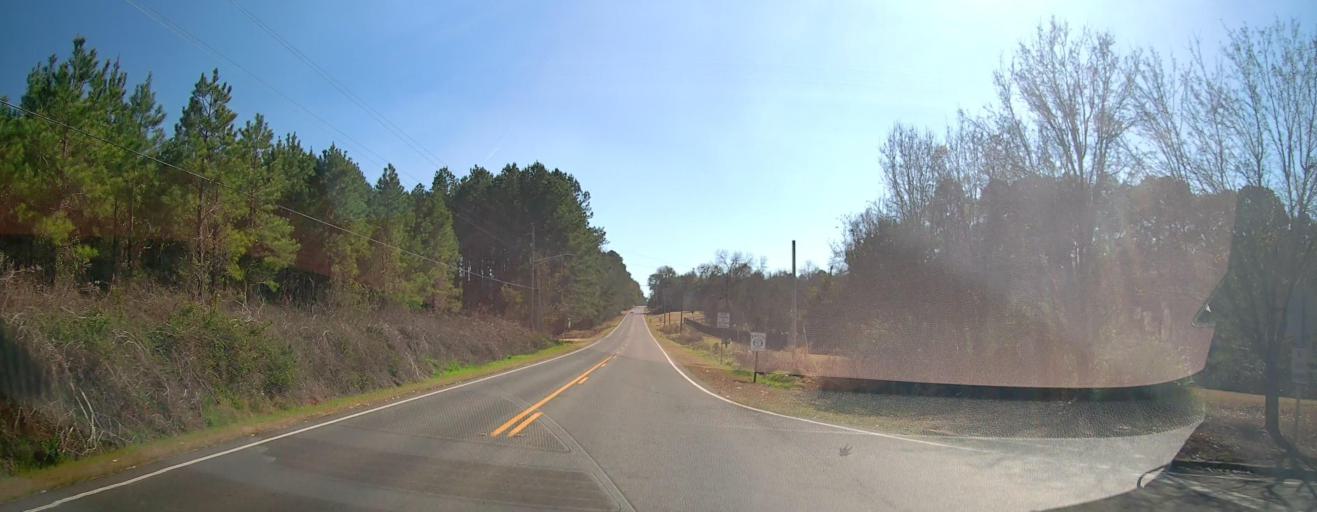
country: US
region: Georgia
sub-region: Macon County
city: Montezuma
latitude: 32.3236
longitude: -84.0226
